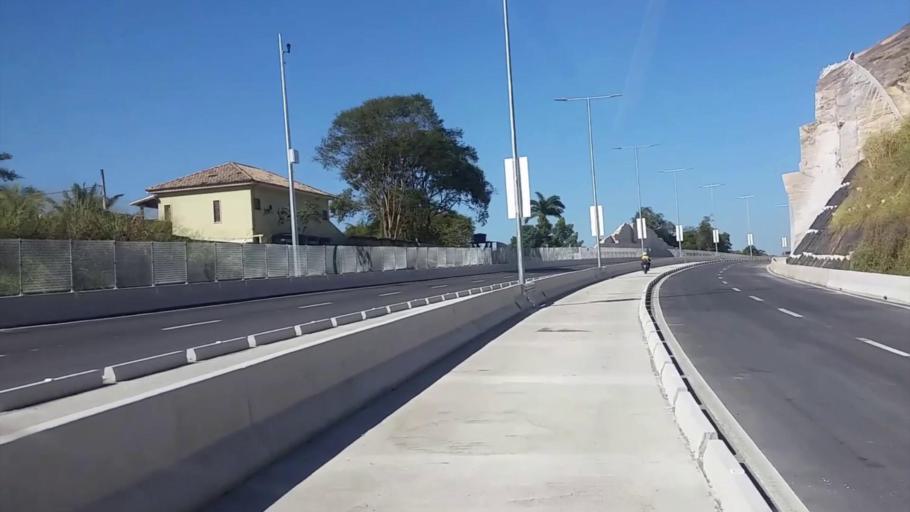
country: BR
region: Rio de Janeiro
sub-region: Nilopolis
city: Nilopolis
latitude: -22.9207
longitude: -43.3968
